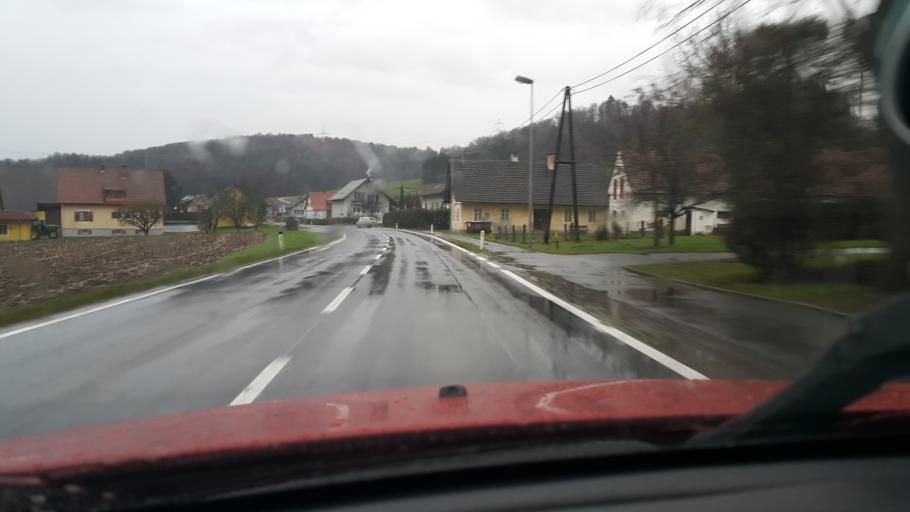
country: AT
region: Styria
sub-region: Politischer Bezirk Leibnitz
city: Wildon
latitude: 46.8681
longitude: 15.4875
